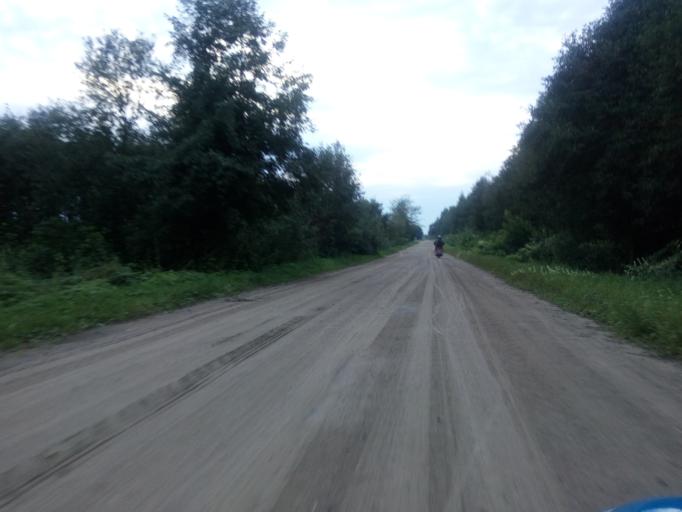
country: BY
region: Vitebsk
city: Dzisna
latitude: 55.6718
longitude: 28.3102
